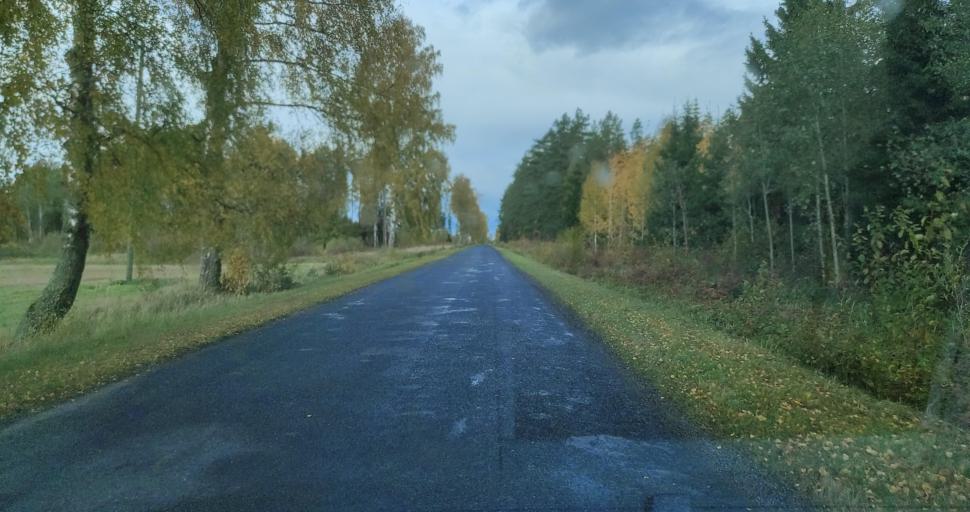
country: LV
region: Skrunda
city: Skrunda
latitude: 56.6833
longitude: 22.0658
